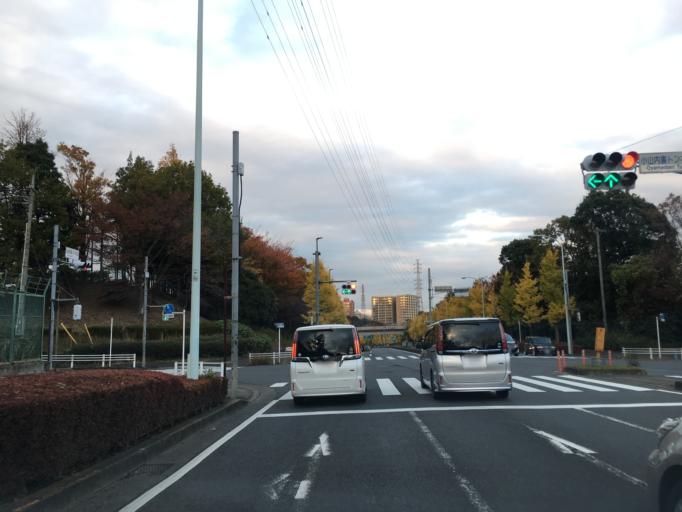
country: JP
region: Tokyo
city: Hachioji
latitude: 35.6088
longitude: 139.3715
